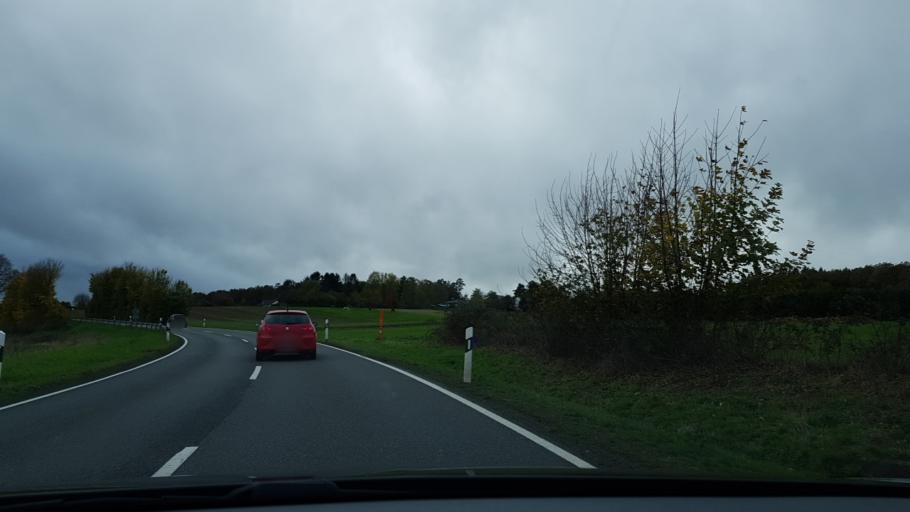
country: DE
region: Rheinland-Pfalz
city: Kalenborn
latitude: 50.5511
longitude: 7.0085
